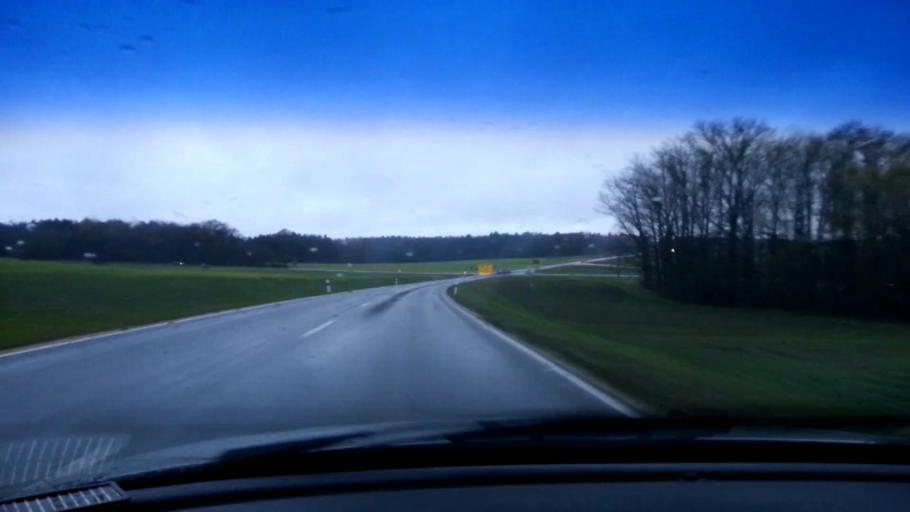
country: DE
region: Bavaria
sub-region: Upper Franconia
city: Zapfendorf
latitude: 49.9977
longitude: 10.9691
